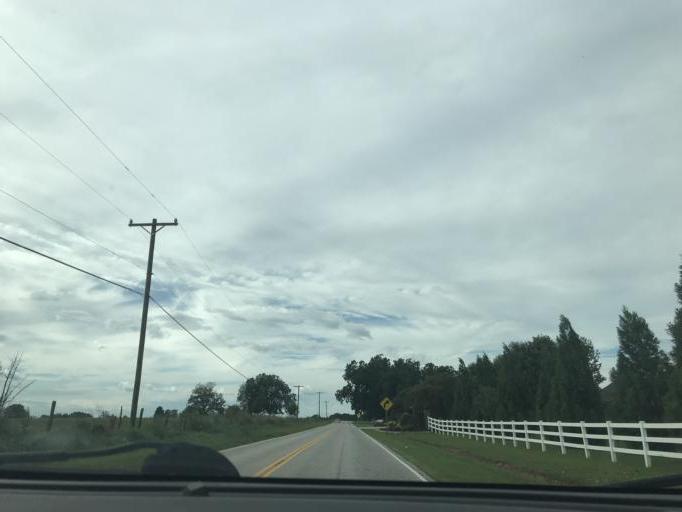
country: US
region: South Carolina
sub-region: Cherokee County
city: East Gaffney
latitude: 35.1285
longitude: -81.6647
